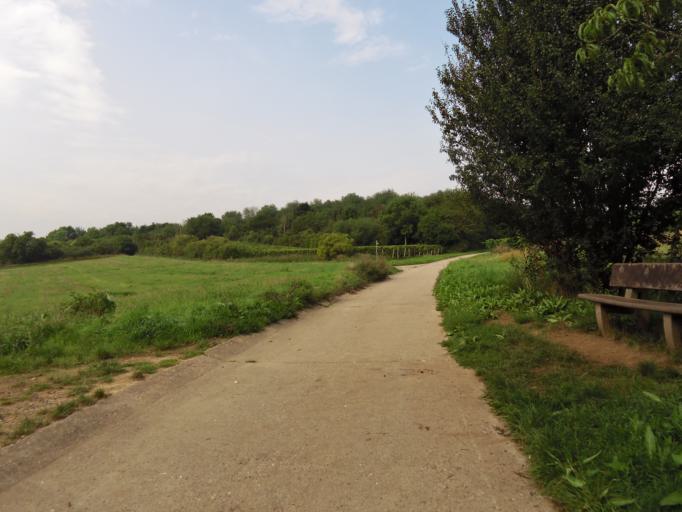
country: DE
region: Rheinland-Pfalz
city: Alzey
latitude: 49.7451
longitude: 8.0924
